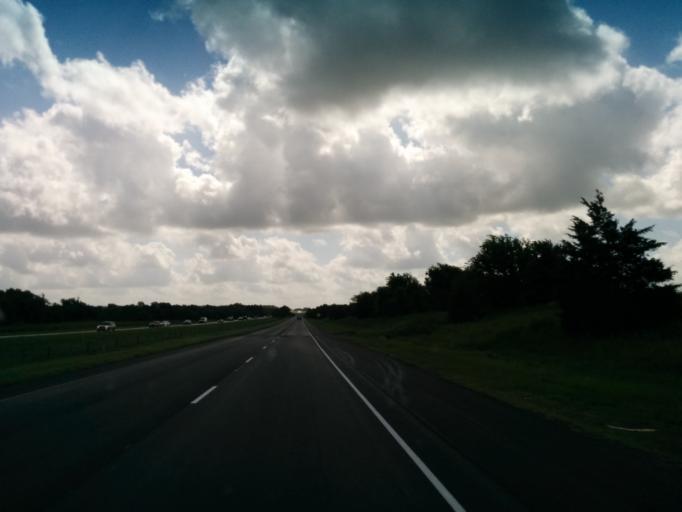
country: US
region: Texas
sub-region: Fayette County
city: Schulenburg
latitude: 29.6959
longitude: -96.8801
